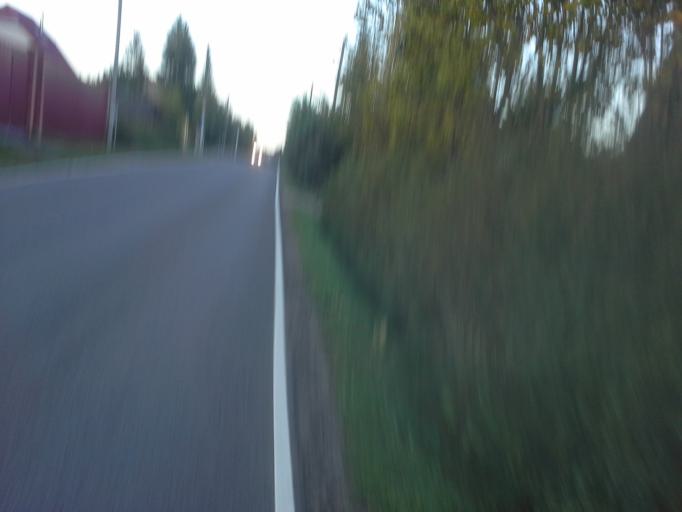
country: RU
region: Moskovskaya
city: Selyatino
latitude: 55.5059
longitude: 36.9332
